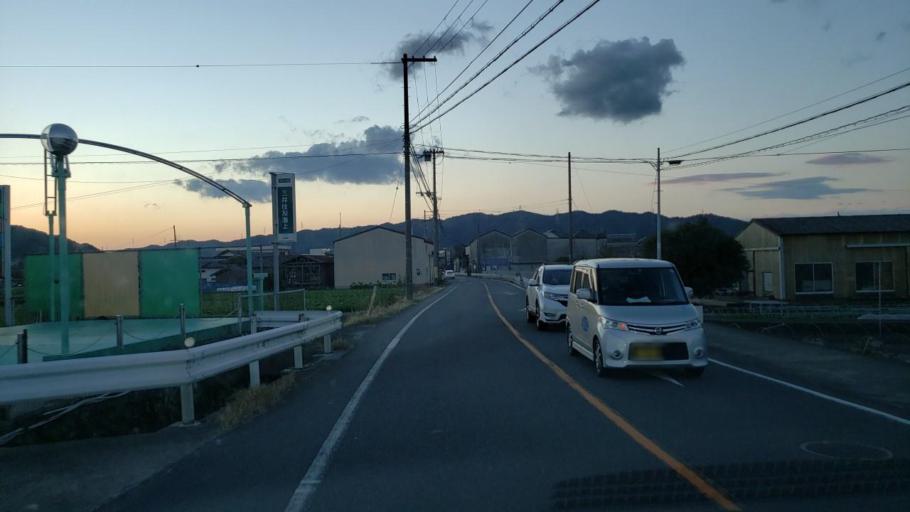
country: JP
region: Hyogo
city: Fukura
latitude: 34.3003
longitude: 134.7589
